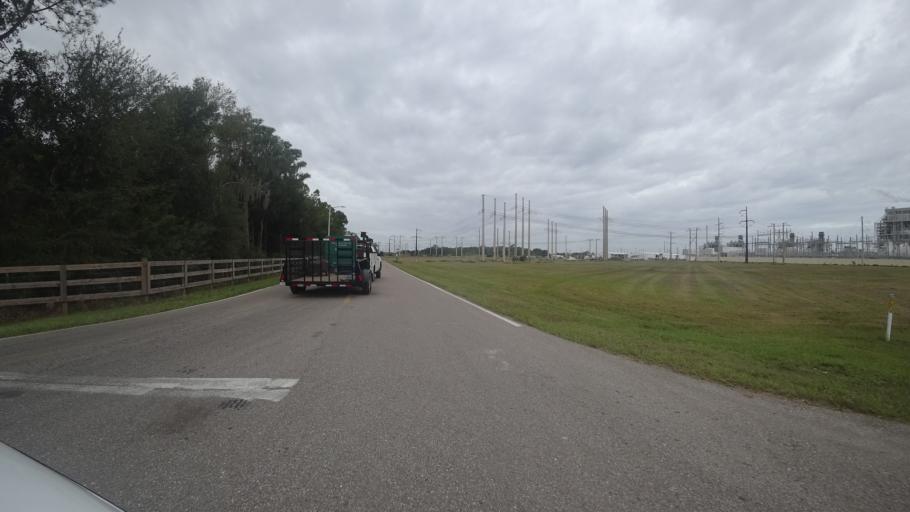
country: US
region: Florida
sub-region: Hillsborough County
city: Sun City Center
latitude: 27.6011
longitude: -82.3442
